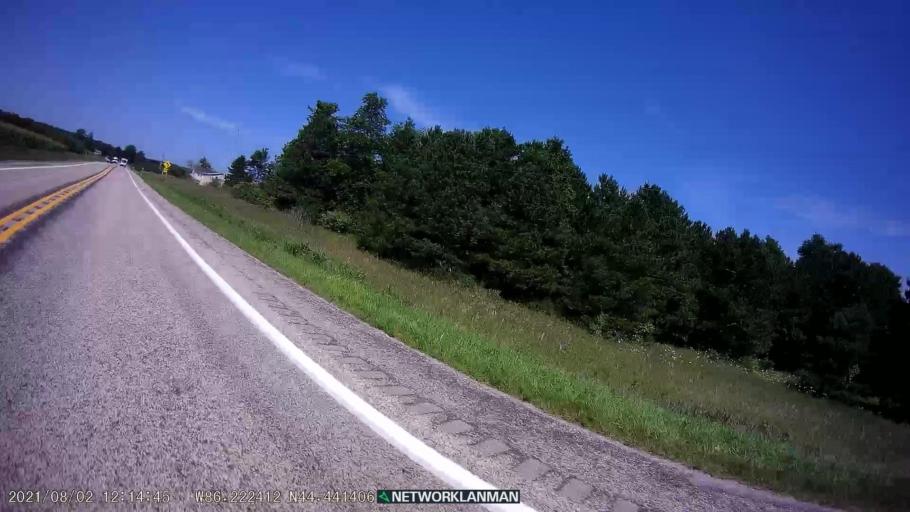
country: US
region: Michigan
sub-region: Benzie County
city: Frankfort
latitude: 44.4418
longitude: -86.2225
